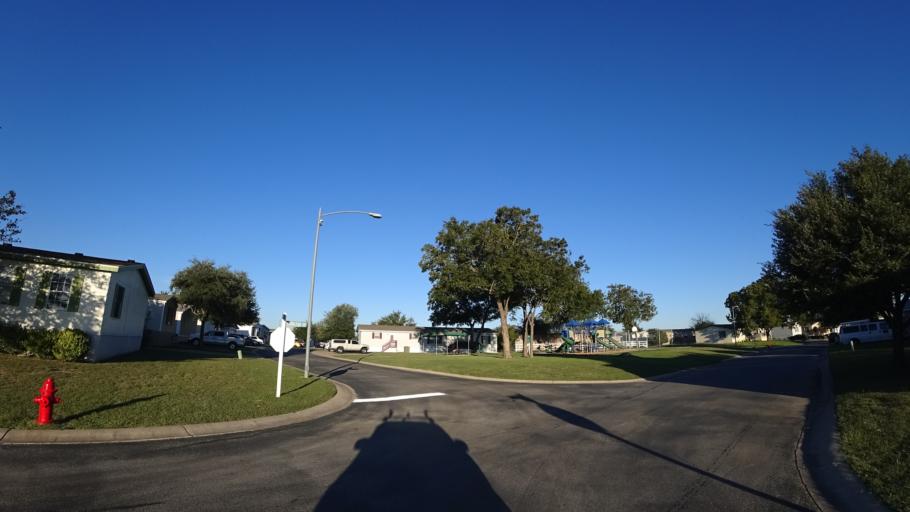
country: US
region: Texas
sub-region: Travis County
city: Manor
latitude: 30.3120
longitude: -97.6263
